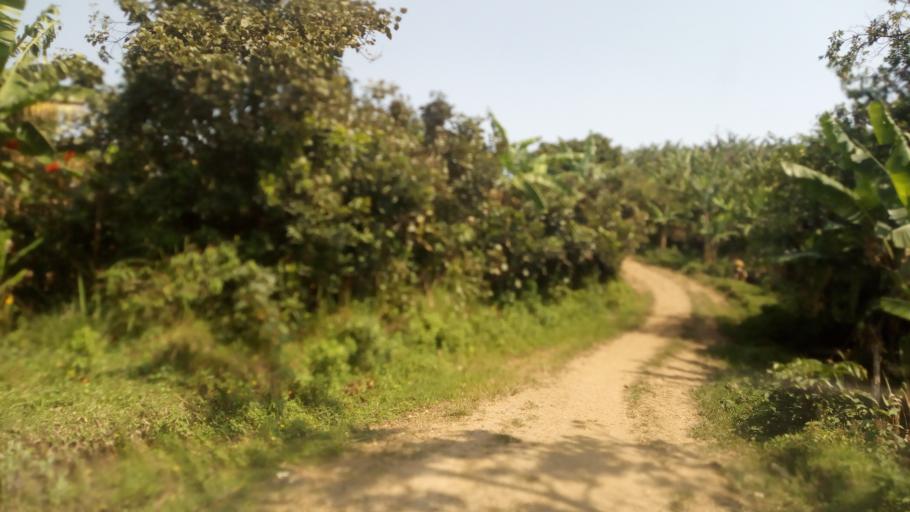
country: UG
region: Western Region
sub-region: Kisoro District
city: Kisoro
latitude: -1.1041
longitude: 29.5909
